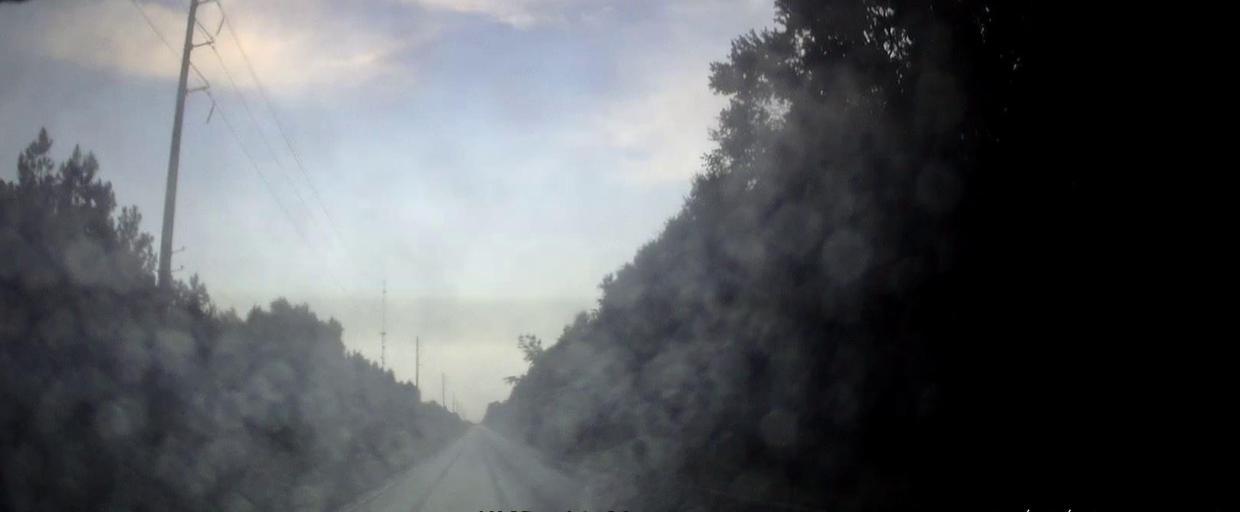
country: US
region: Georgia
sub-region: Dodge County
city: Chester
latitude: 32.5681
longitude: -83.1811
